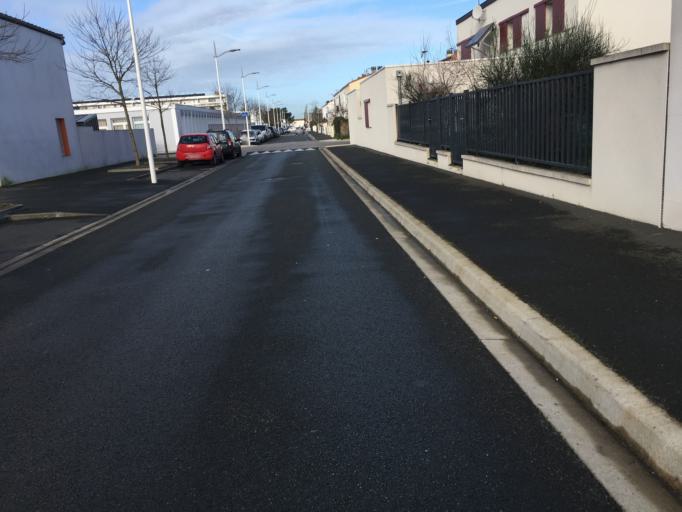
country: FR
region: Poitou-Charentes
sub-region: Departement de la Charente-Maritime
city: La Rochelle
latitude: 46.1714
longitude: -1.1773
